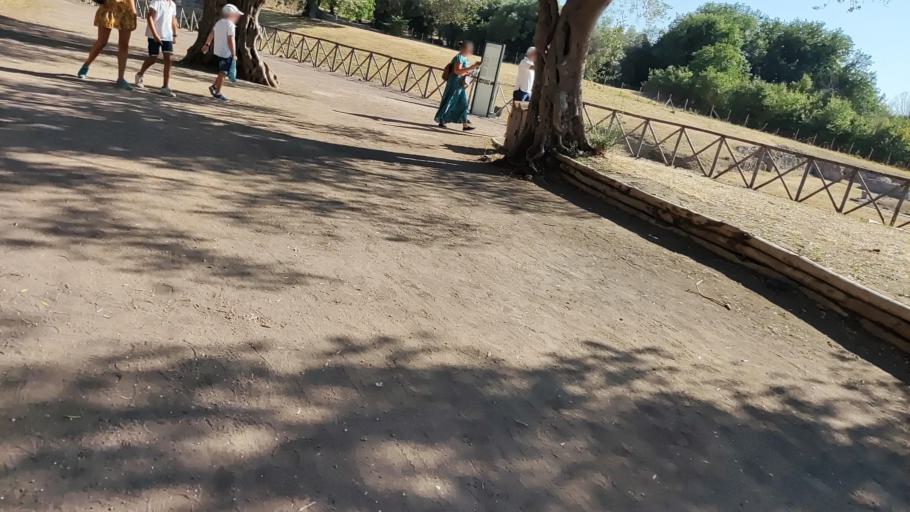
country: IT
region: Latium
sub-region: Citta metropolitana di Roma Capitale
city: Villa Adriana
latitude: 41.9410
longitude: 12.7745
